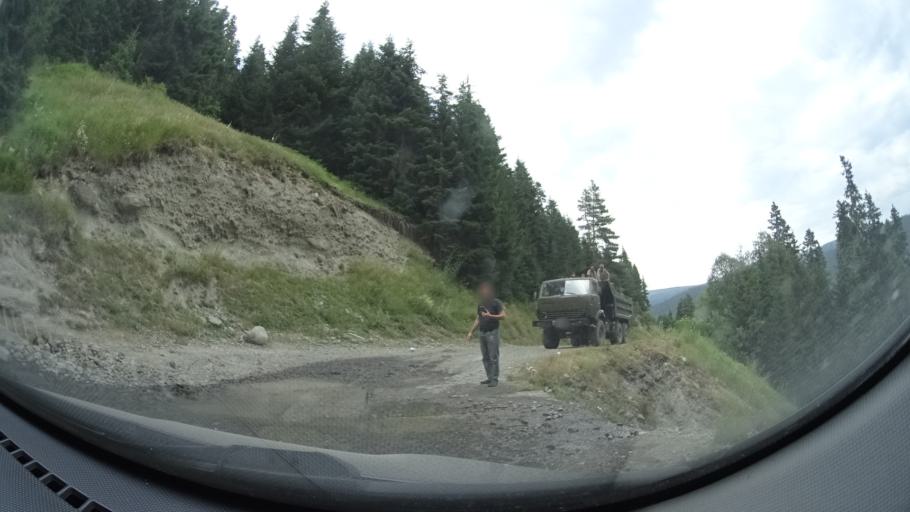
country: GE
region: Samtskhe-Javakheti
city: Adigeni
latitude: 41.6392
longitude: 42.5830
